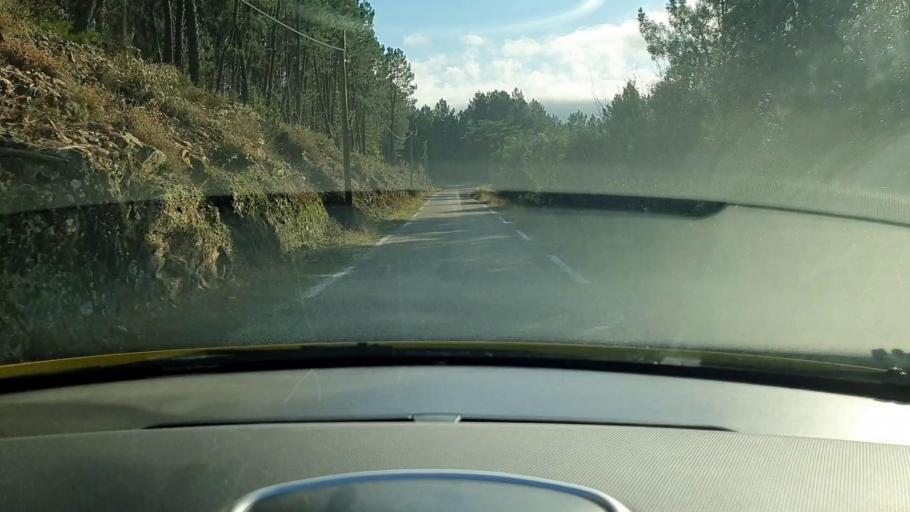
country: FR
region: Languedoc-Roussillon
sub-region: Departement du Gard
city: Besseges
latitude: 44.3115
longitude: 4.0065
